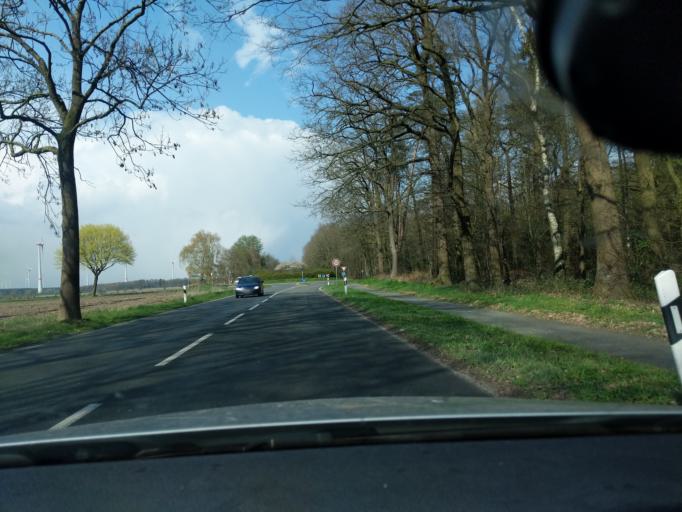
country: DE
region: Lower Saxony
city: Harsefeld
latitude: 53.4738
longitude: 9.4936
